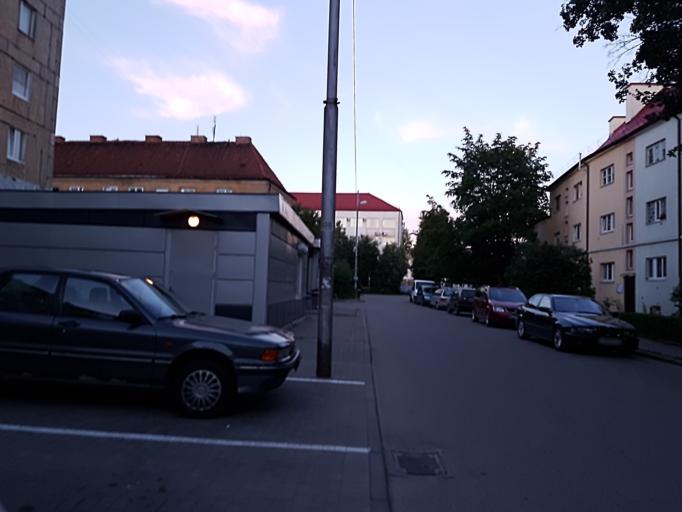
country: RU
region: Kaliningrad
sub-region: Gorod Kaliningrad
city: Kaliningrad
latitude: 54.6891
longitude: 20.5221
